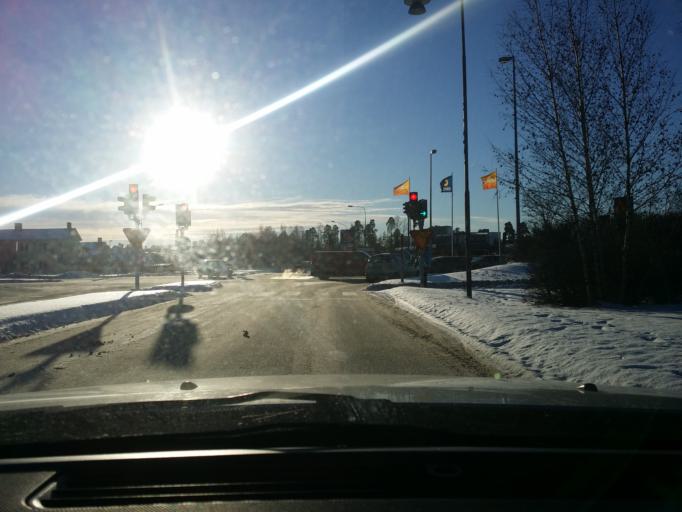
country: SE
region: Vaestmanland
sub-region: Vasteras
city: Vasteras
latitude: 59.6156
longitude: 16.5770
